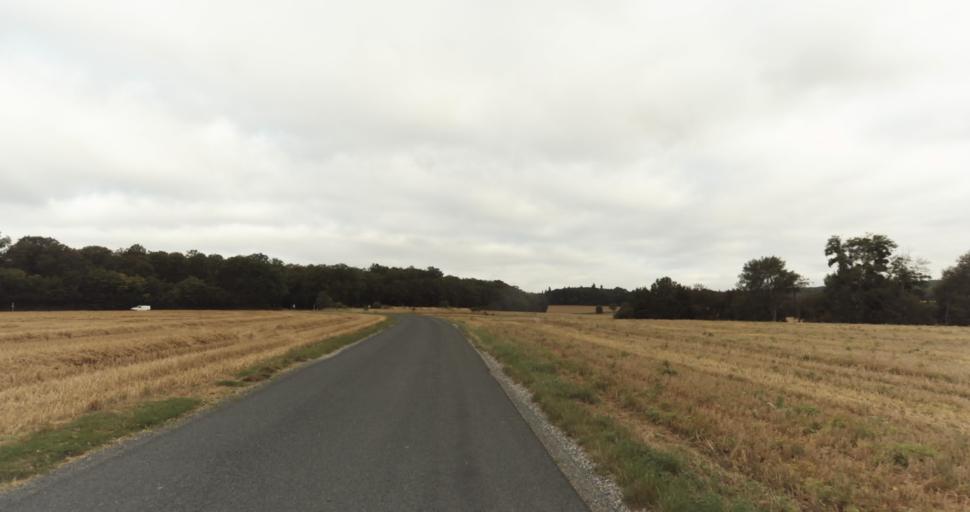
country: FR
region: Centre
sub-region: Departement d'Eure-et-Loir
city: Saint-Remy-sur-Avre
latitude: 48.7762
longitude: 1.2455
